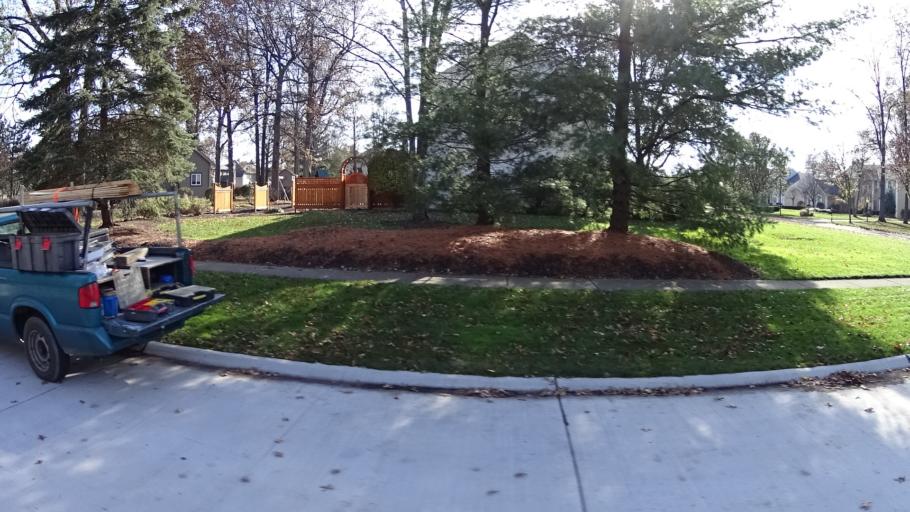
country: US
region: Ohio
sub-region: Lorain County
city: Avon Lake
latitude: 41.4975
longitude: -81.9756
